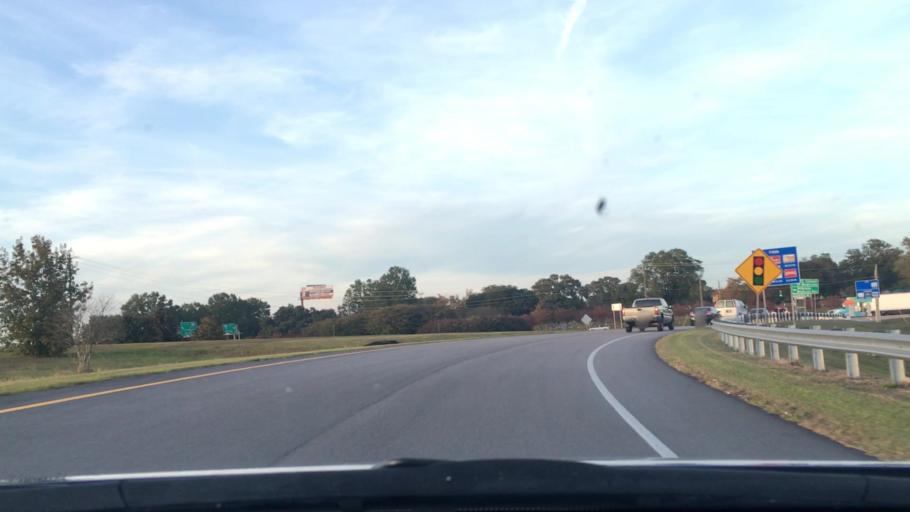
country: US
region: South Carolina
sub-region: Richland County
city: Forest Acres
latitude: 33.9712
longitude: -80.9539
